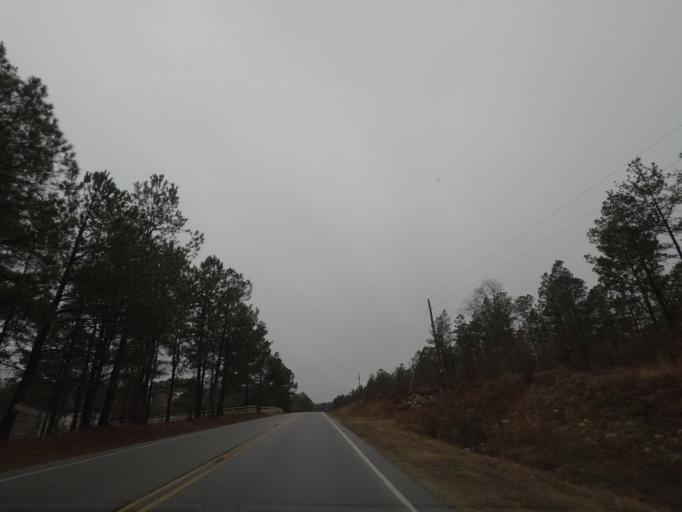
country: US
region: North Carolina
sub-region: Cumberland County
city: Spring Lake
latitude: 35.2779
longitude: -78.9878
